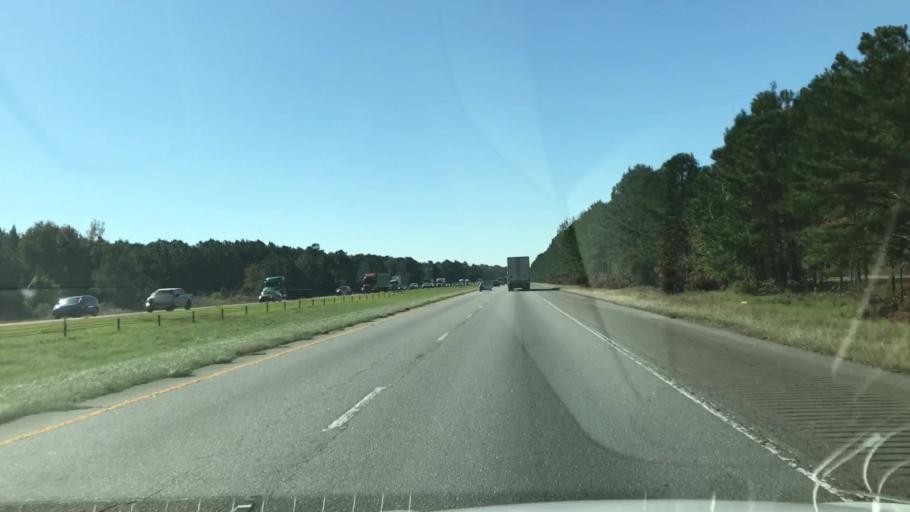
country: US
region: South Carolina
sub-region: Hampton County
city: Yemassee
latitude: 32.6122
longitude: -80.8946
